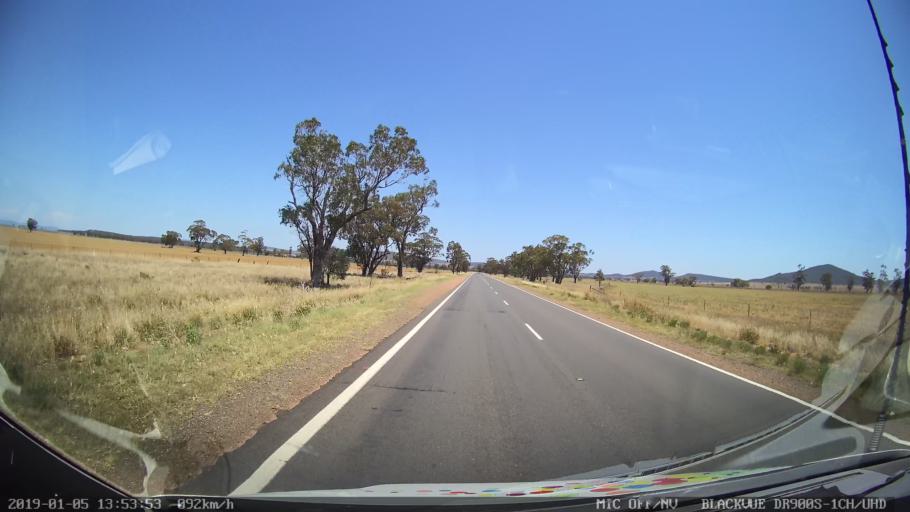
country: AU
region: New South Wales
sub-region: Gunnedah
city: Gunnedah
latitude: -31.0809
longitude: 150.2759
